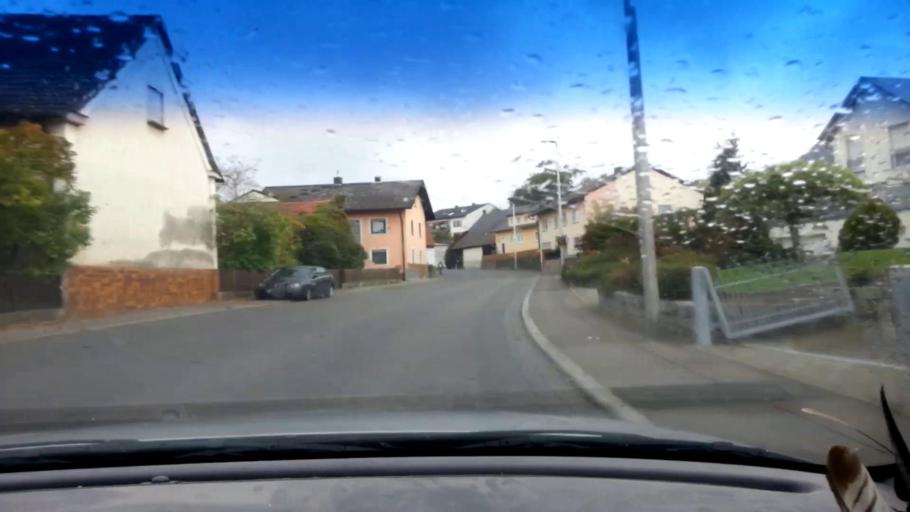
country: DE
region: Bavaria
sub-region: Upper Franconia
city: Stegaurach
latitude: 49.8643
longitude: 10.8398
